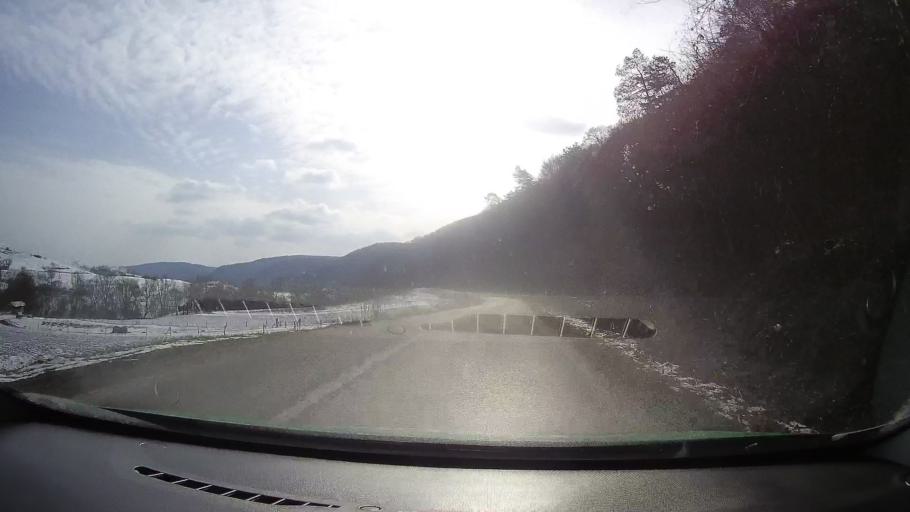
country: RO
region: Mures
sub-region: Comuna Apold
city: Saes
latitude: 46.1843
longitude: 24.7611
